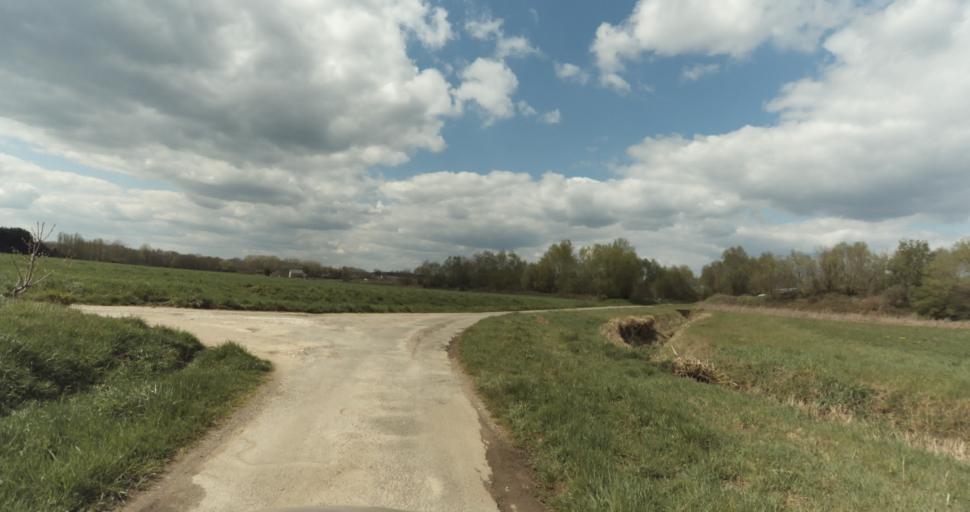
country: FR
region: Bourgogne
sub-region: Departement de la Cote-d'Or
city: Auxonne
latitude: 47.1761
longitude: 5.3998
